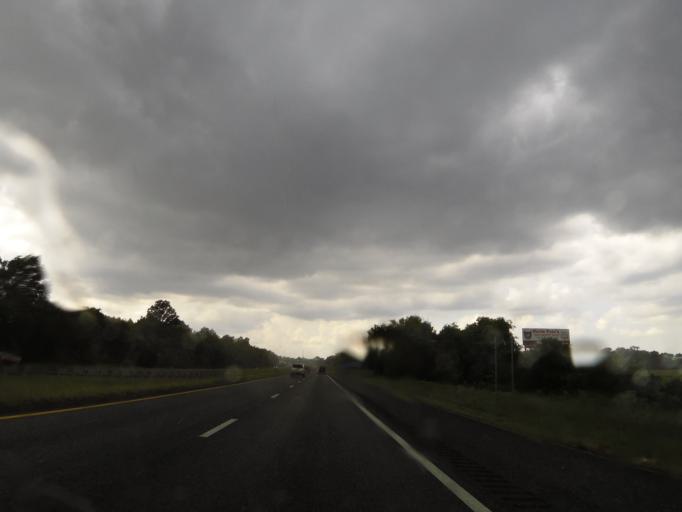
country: US
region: Tennessee
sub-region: Wilson County
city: Lebanon
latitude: 36.1938
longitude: -86.2381
